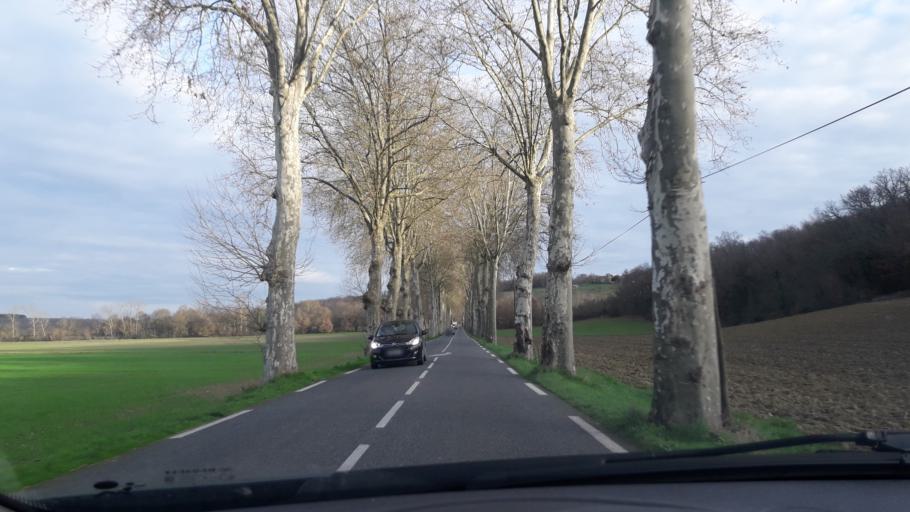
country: FR
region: Midi-Pyrenees
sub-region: Departement de la Haute-Garonne
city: Daux
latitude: 43.7154
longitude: 1.2486
